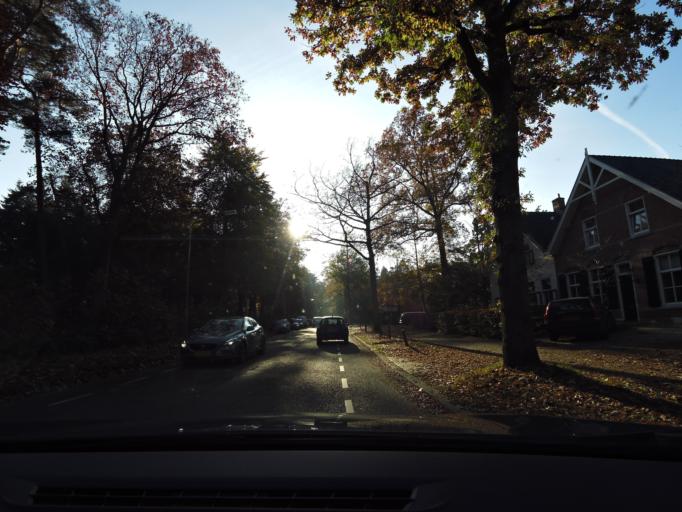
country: NL
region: North Brabant
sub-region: Gemeente Breda
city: Breda
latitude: 51.5658
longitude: 4.7741
